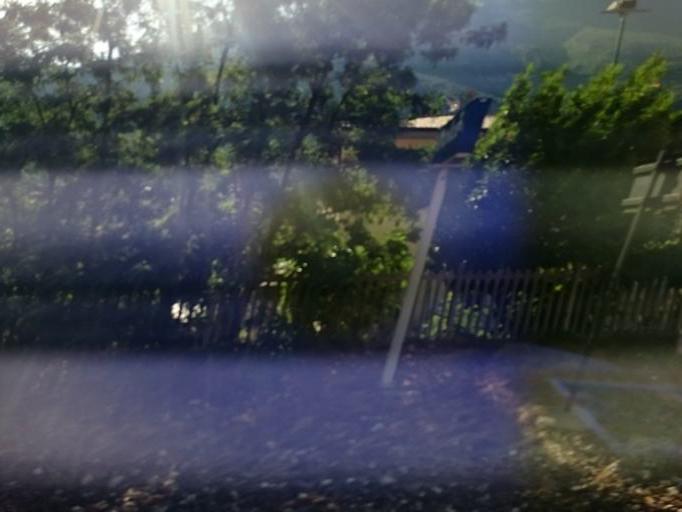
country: IT
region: Veneto
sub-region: Provincia di Verona
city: Dolce
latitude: 45.6019
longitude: 10.8508
